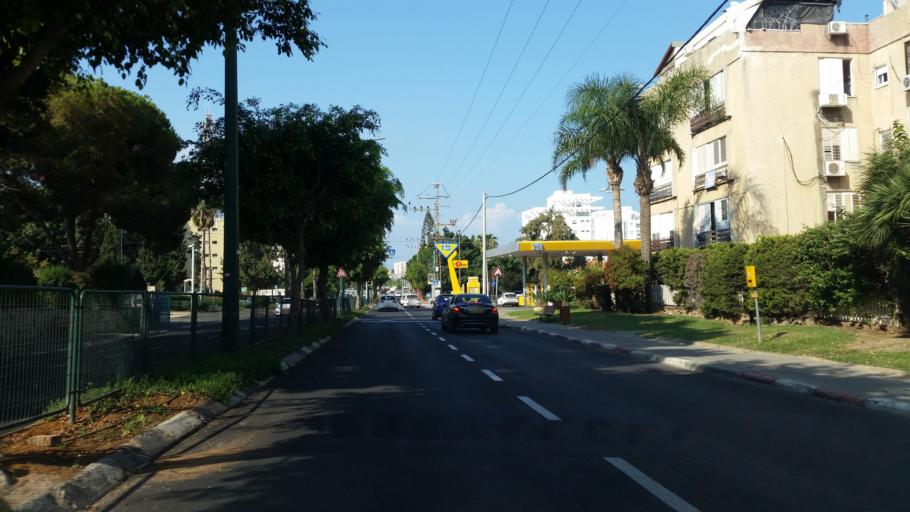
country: IL
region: Tel Aviv
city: Herzliyya
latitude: 32.1630
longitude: 34.8309
